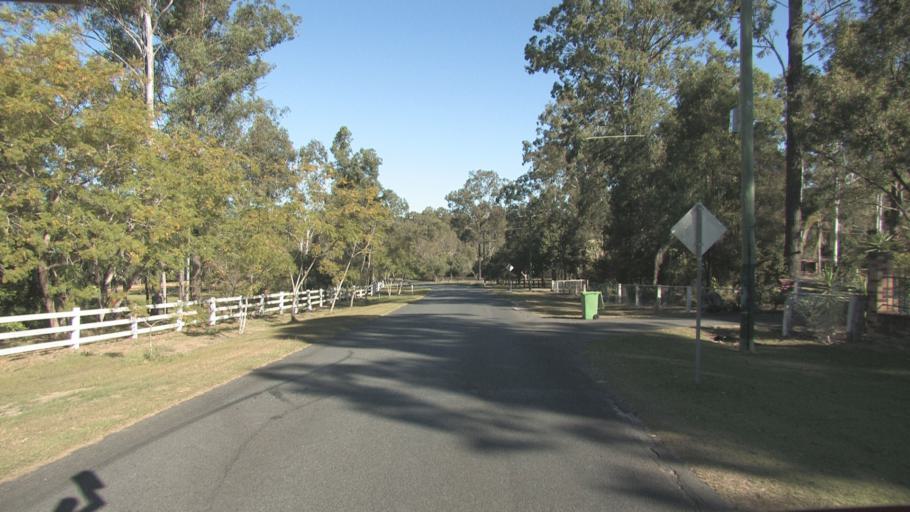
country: AU
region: Queensland
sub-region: Logan
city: Park Ridge South
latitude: -27.7277
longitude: 153.0201
